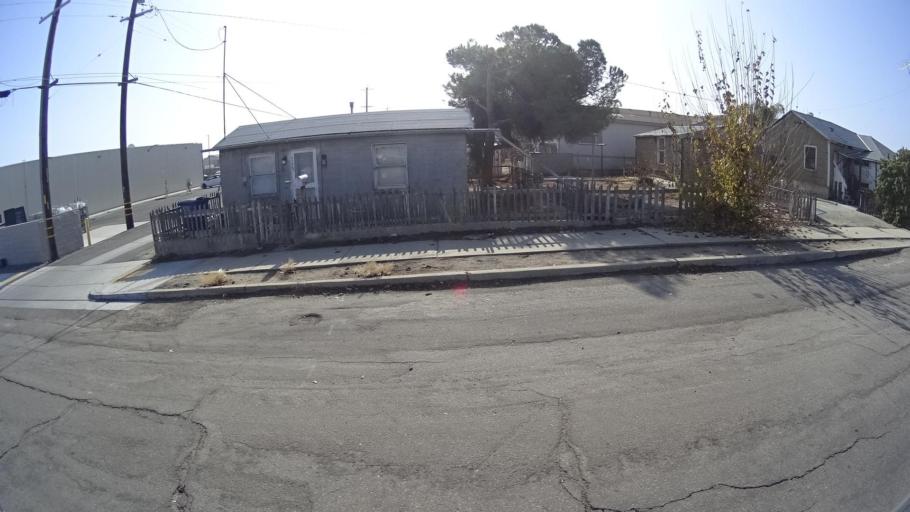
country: US
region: California
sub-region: Kern County
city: Ford City
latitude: 35.1576
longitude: -119.4572
